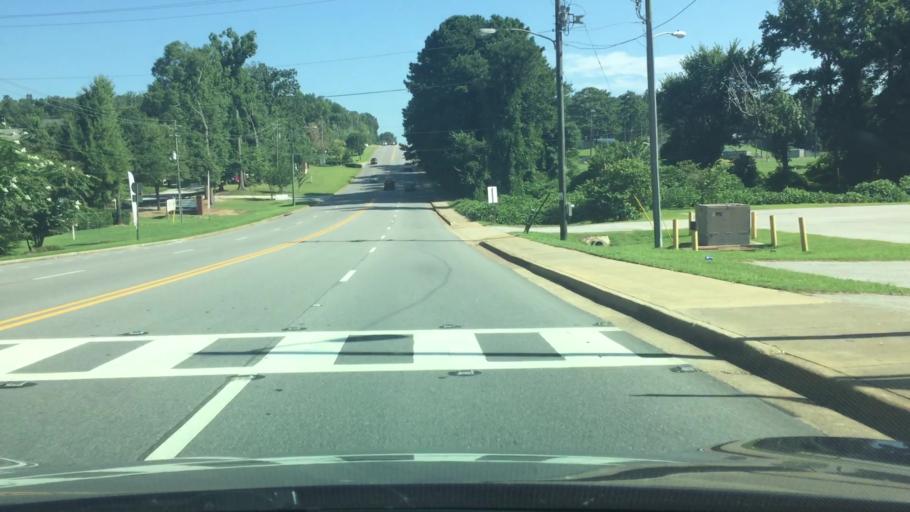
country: US
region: Alabama
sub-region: Lee County
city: Auburn
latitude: 32.6106
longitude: -85.4476
